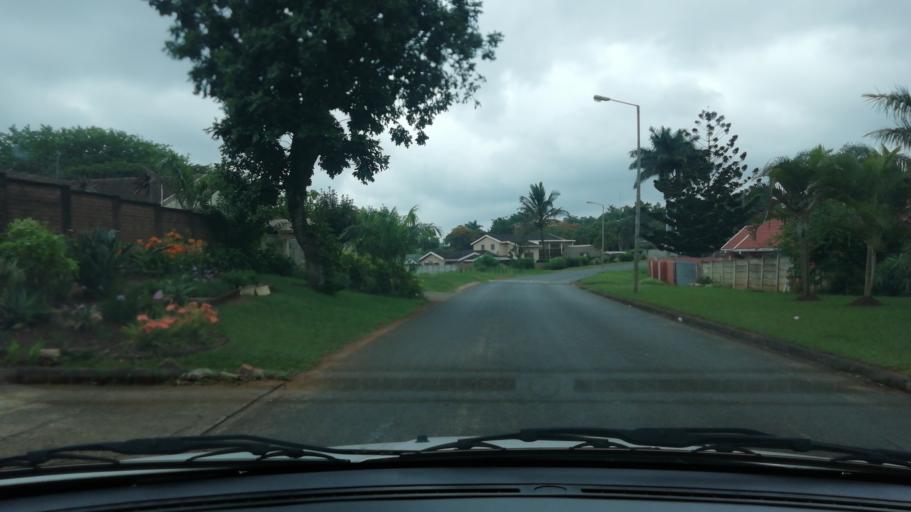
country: ZA
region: KwaZulu-Natal
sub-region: uThungulu District Municipality
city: Empangeni
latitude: -28.7624
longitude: 31.9006
